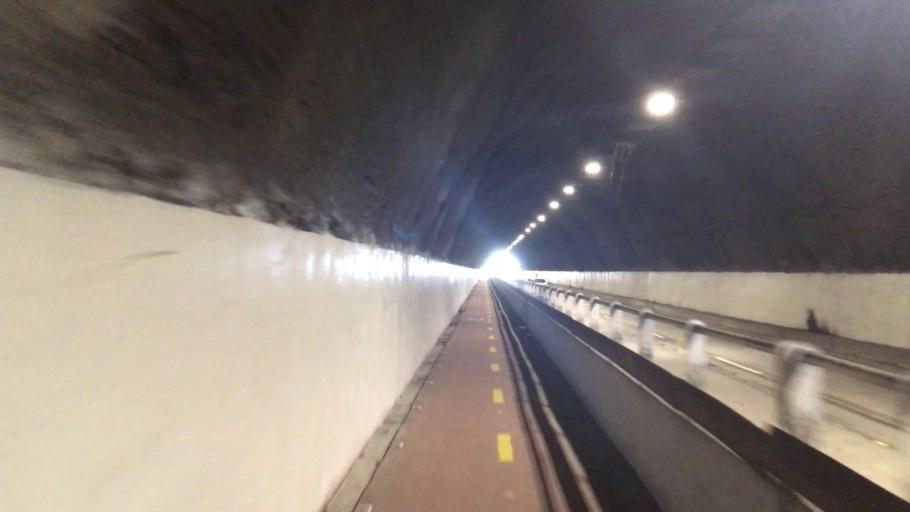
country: BR
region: Rio de Janeiro
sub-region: Rio De Janeiro
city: Rio de Janeiro
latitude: -23.0107
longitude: -43.2890
